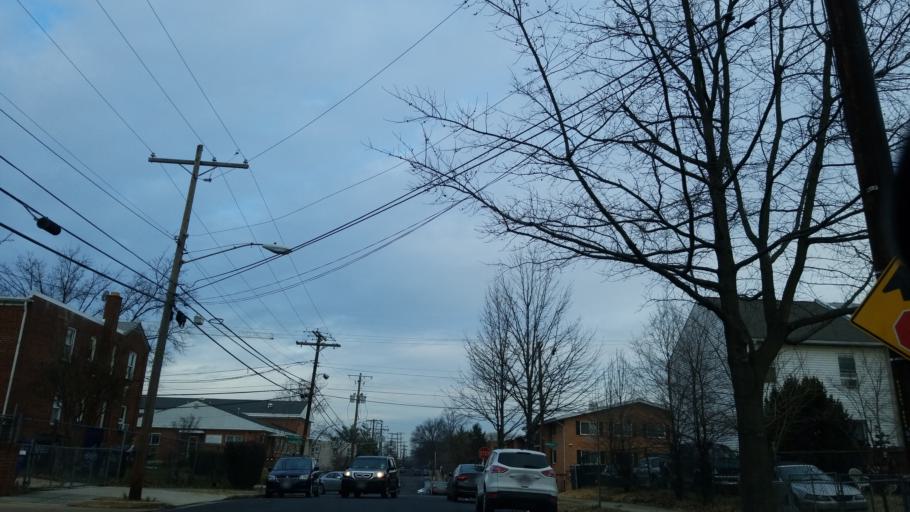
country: US
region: Maryland
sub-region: Prince George's County
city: Glassmanor
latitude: 38.8313
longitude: -76.9895
